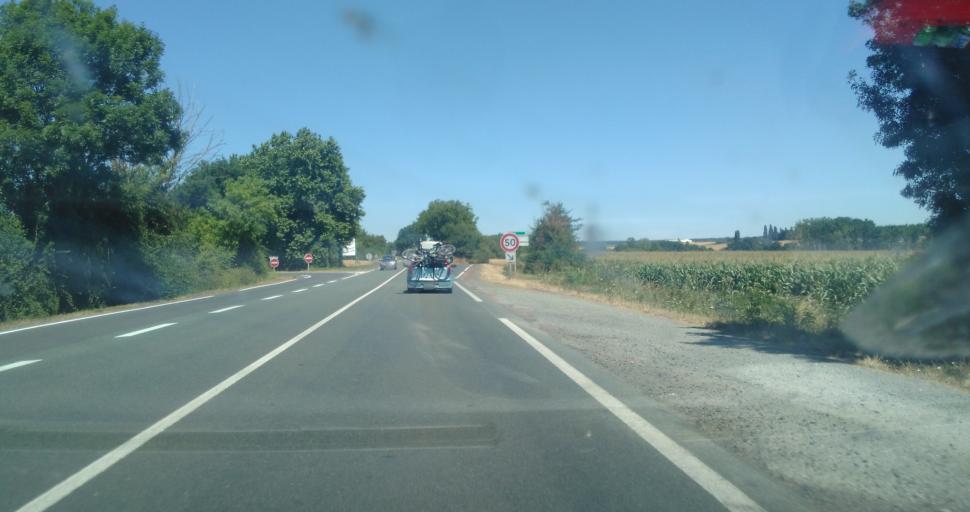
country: FR
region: Pays de la Loire
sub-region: Departement de la Vendee
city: Sainte-Hermine
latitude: 46.5687
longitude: -1.0551
